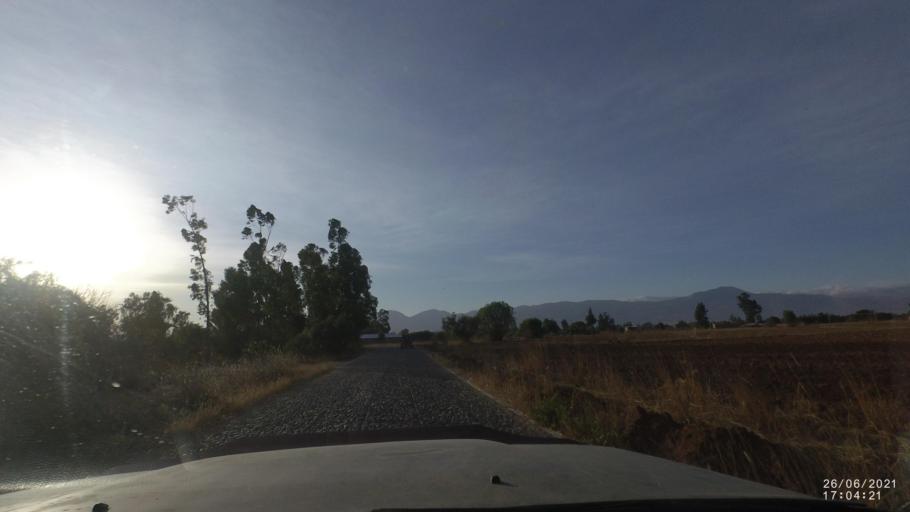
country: BO
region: Cochabamba
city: Cliza
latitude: -17.6360
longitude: -65.9164
